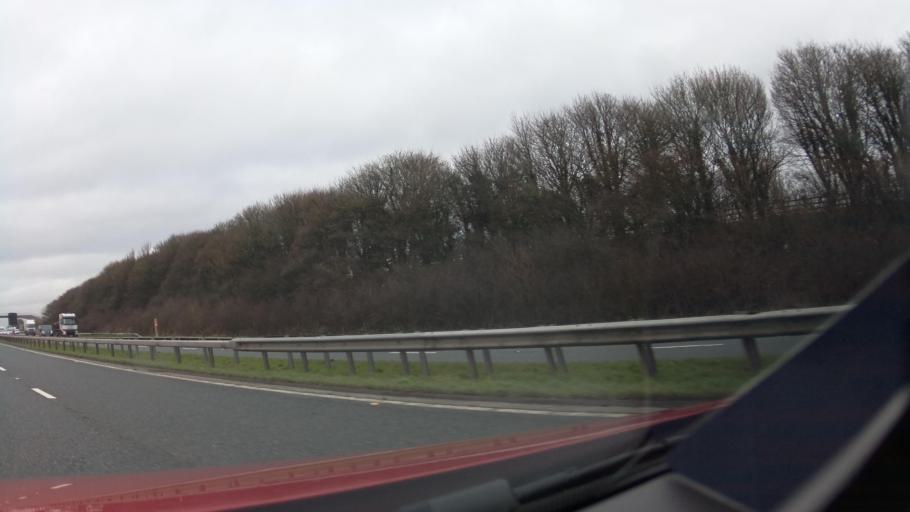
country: GB
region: England
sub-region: Lancashire
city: Goosnargh
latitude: 53.8216
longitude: -2.7161
